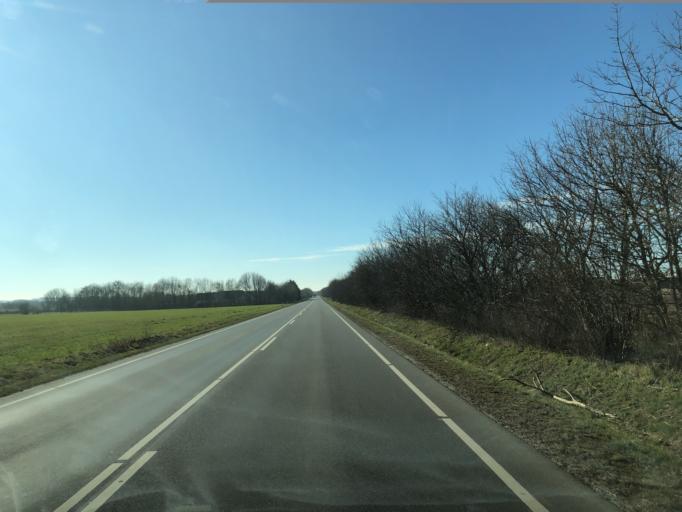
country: DK
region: Central Jutland
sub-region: Ikast-Brande Kommune
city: Bording Kirkeby
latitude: 56.1514
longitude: 9.2294
